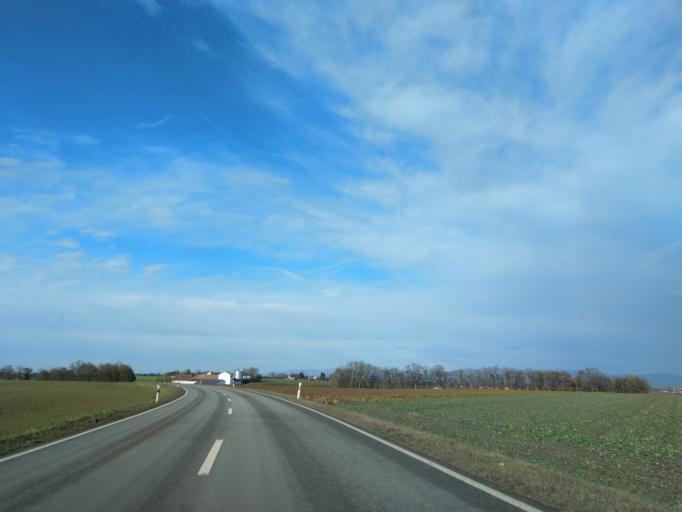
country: DE
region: Bavaria
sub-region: Lower Bavaria
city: Kunzing
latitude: 48.6597
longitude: 13.0454
